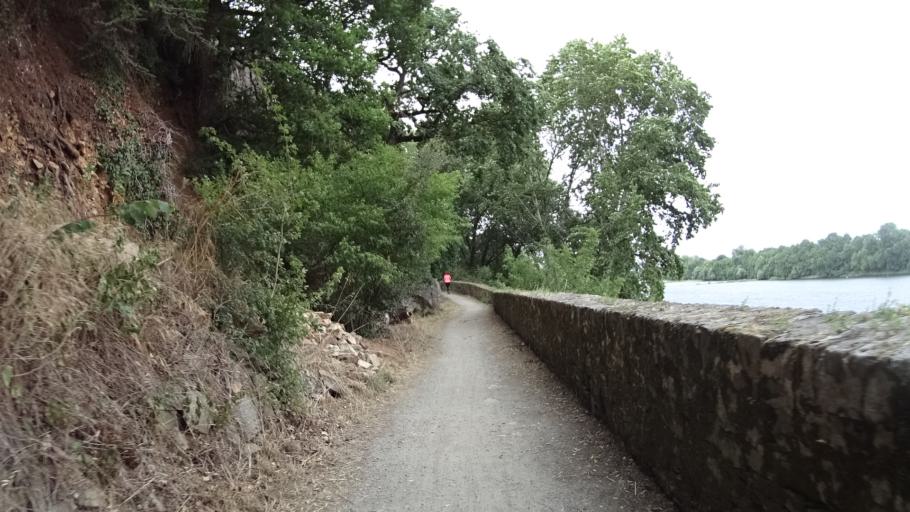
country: FR
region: Pays de la Loire
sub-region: Departement de la Loire-Atlantique
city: Le Cellier
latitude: 47.3240
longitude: -1.3318
